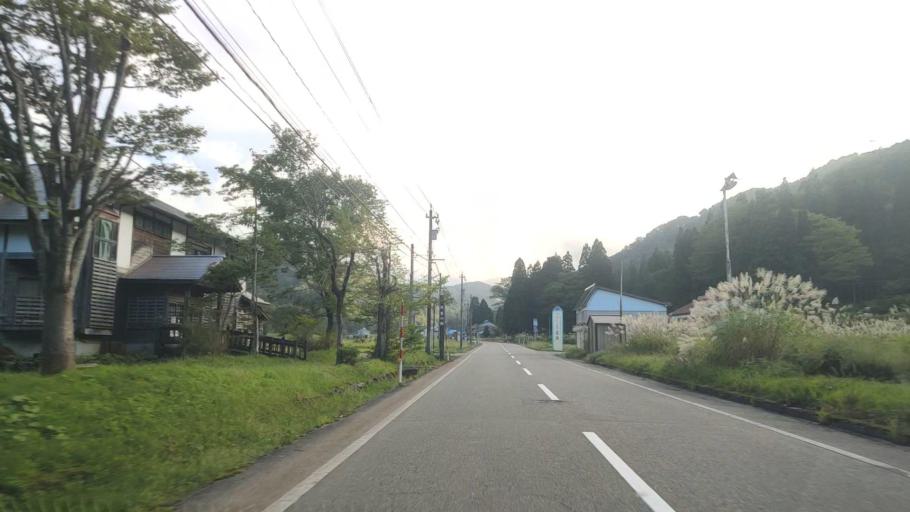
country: JP
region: Toyama
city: Yatsuomachi-higashikumisaka
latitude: 36.4578
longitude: 137.0422
